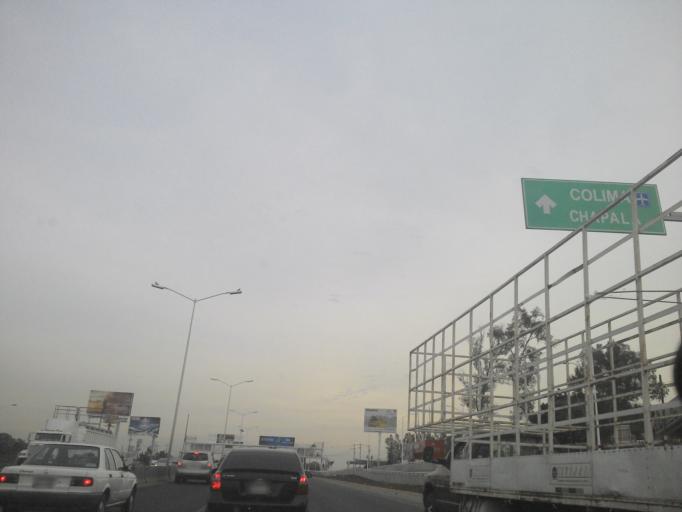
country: MX
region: Jalisco
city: Guadalajara
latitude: 20.6719
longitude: -103.4544
